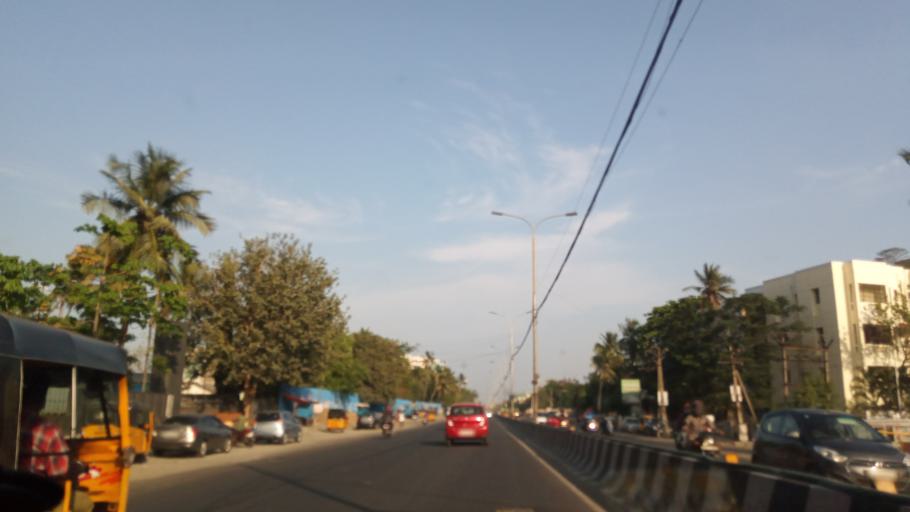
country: IN
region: Tamil Nadu
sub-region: Thiruvallur
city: Porur
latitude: 13.0318
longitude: 80.1645
